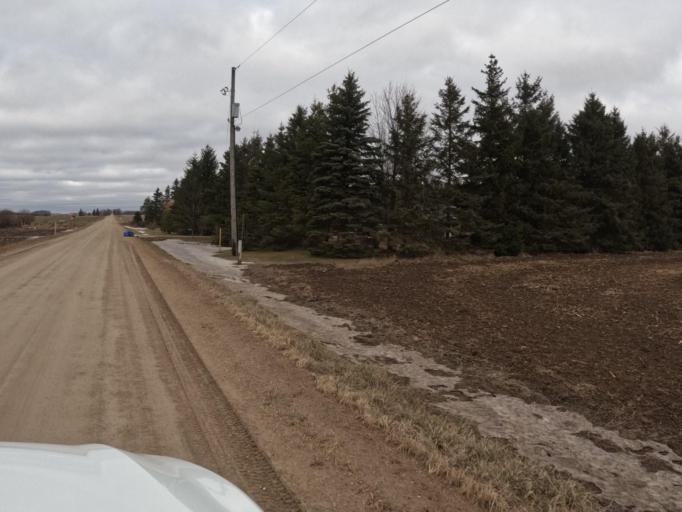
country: CA
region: Ontario
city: Shelburne
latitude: 43.8668
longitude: -80.4011
